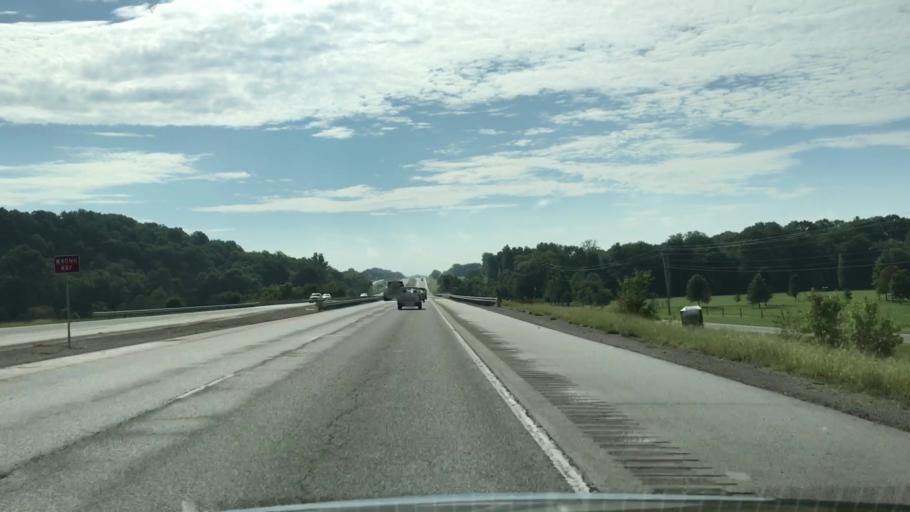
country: US
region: Kentucky
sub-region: Warren County
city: Plano
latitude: 36.8984
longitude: -86.3846
